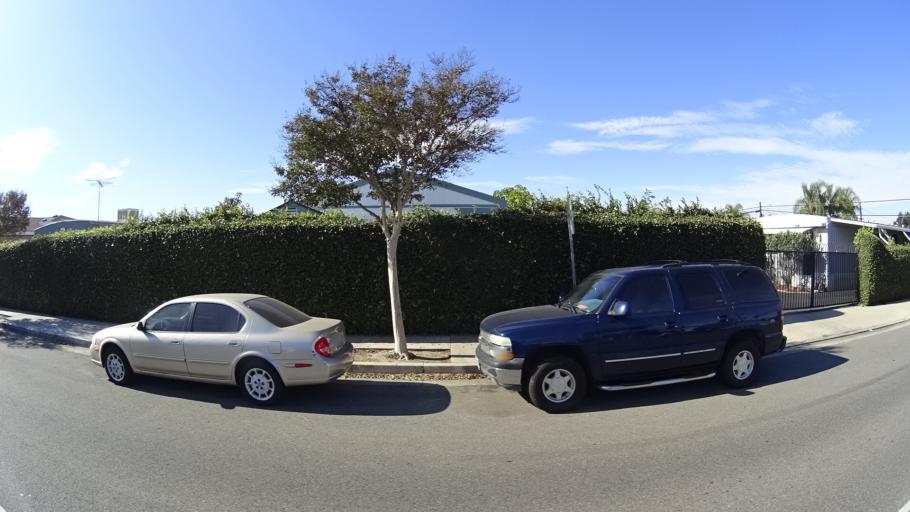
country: US
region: California
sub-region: Orange County
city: Garden Grove
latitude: 33.7778
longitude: -117.9236
